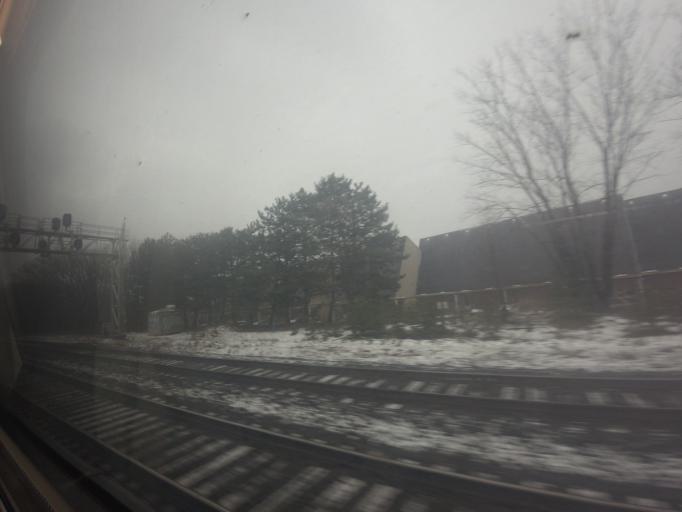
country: CA
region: Ontario
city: Toronto
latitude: 43.6750
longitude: -79.3293
